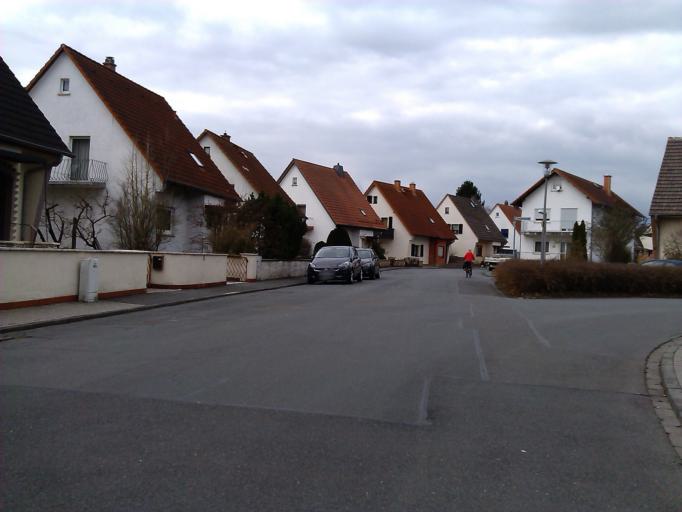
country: DE
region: Hesse
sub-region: Regierungsbezirk Darmstadt
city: Nauheim
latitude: 49.9467
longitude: 8.4434
